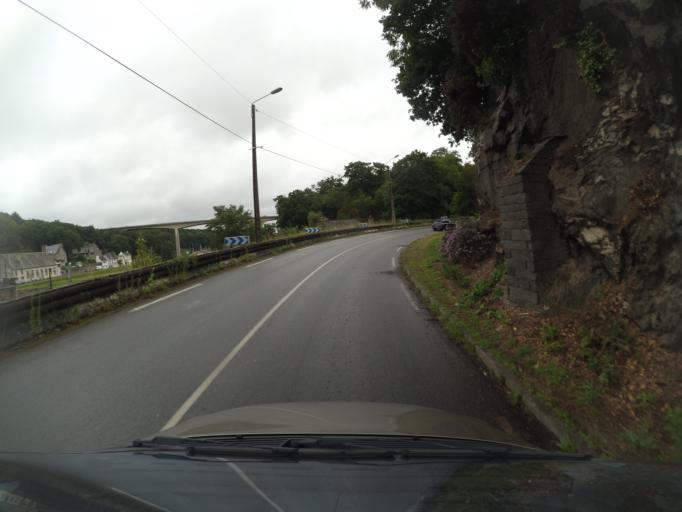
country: FR
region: Brittany
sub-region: Departement du Finistere
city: Morlaix
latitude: 48.5890
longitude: -3.8374
